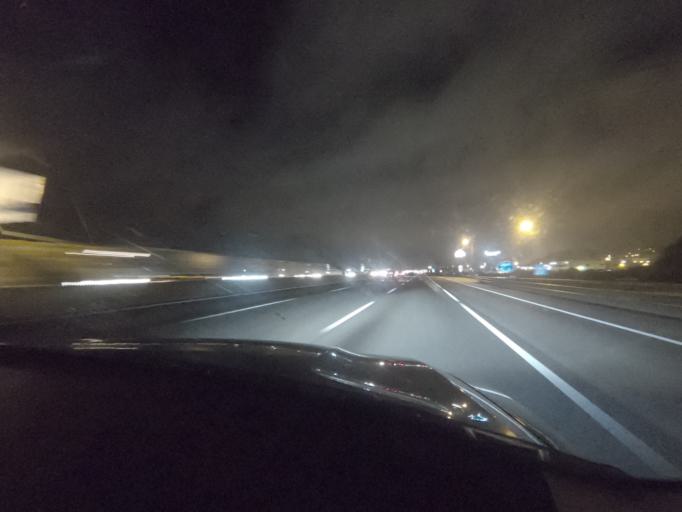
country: PT
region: Lisbon
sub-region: Vila Franca de Xira
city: Castanheira do Ribatejo
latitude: 39.0042
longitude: -8.9672
